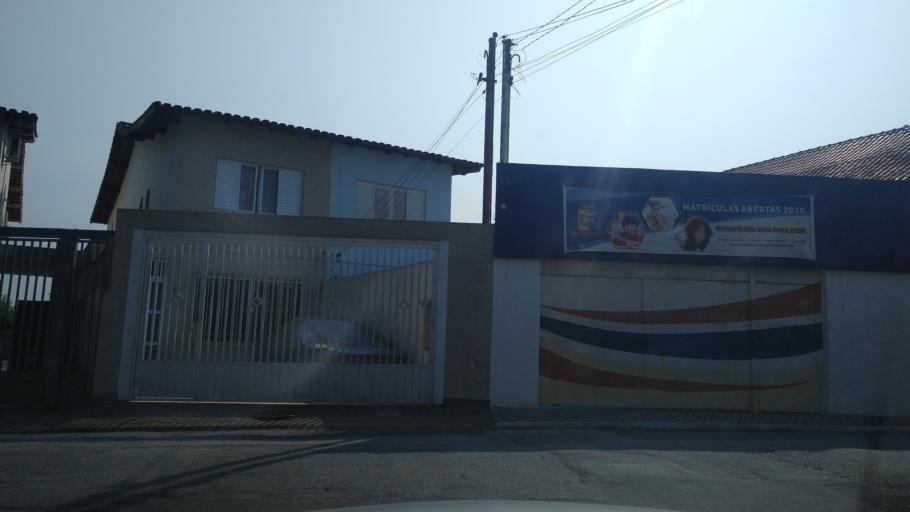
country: BR
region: Sao Paulo
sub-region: Sao Paulo
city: Sao Paulo
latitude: -23.4826
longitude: -46.6249
